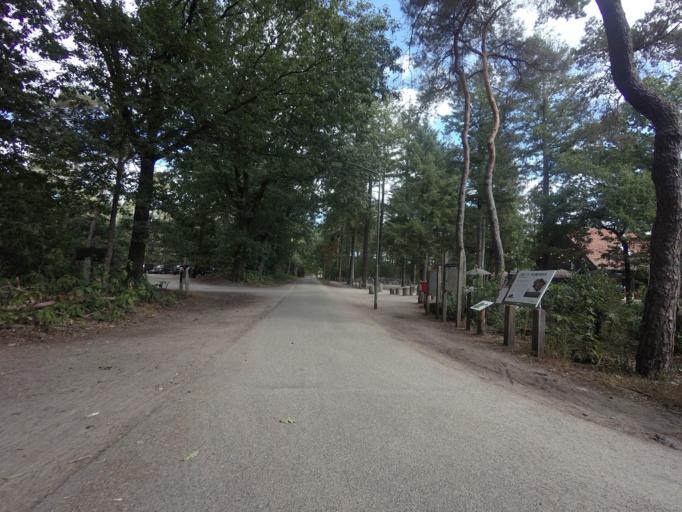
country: NL
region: North Brabant
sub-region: Gemeente Landerd
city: Schaijk
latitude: 51.7263
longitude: 5.6309
